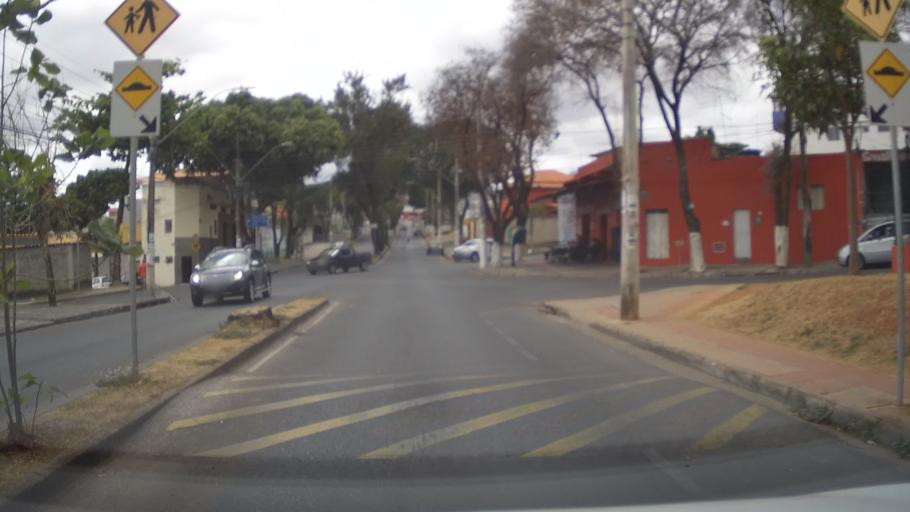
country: BR
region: Minas Gerais
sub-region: Belo Horizonte
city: Belo Horizonte
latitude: -19.8350
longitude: -43.9331
